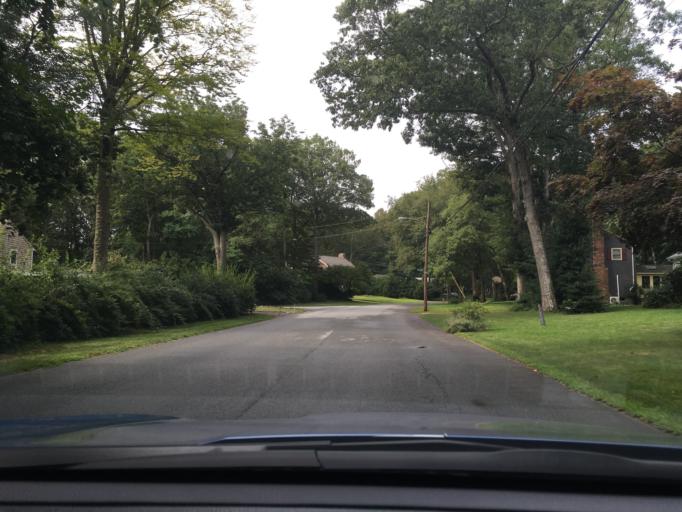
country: US
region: Rhode Island
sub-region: Kent County
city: East Greenwich
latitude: 41.6569
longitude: -71.4733
